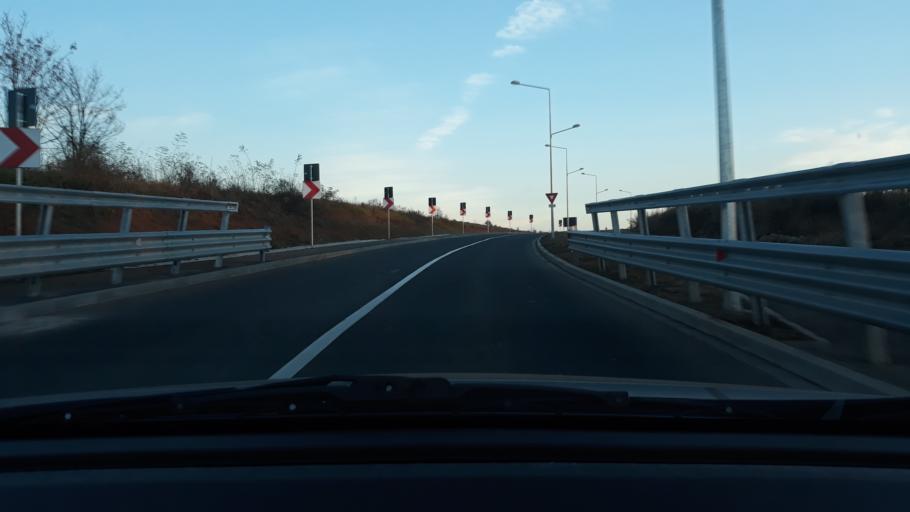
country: RO
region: Bihor
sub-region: Comuna Biharea
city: Biharea
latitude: 47.1109
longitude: 21.9045
